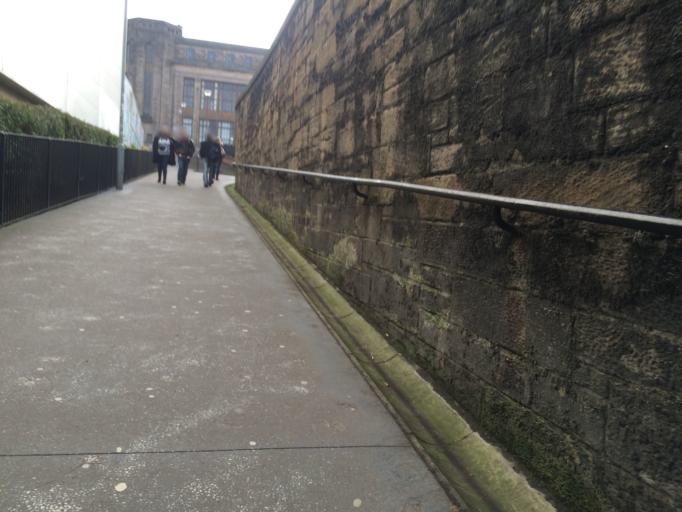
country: GB
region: Scotland
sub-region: Edinburgh
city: Edinburgh
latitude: 55.9410
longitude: -3.2190
